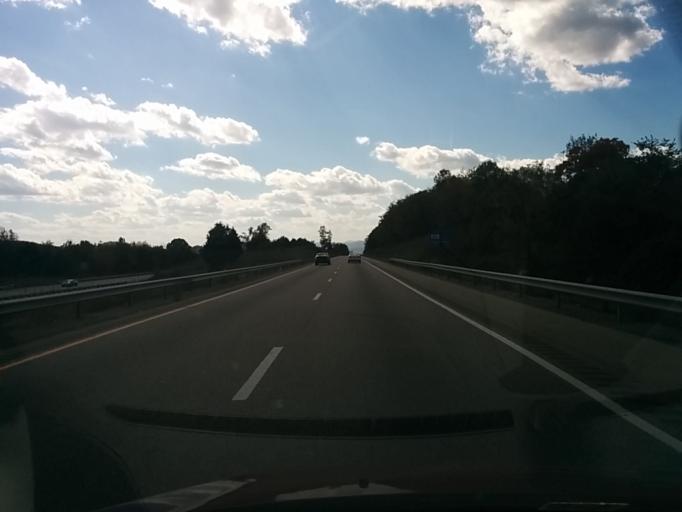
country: US
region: Virginia
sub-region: Rockbridge County
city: East Lexington
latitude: 37.8646
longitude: -79.3385
